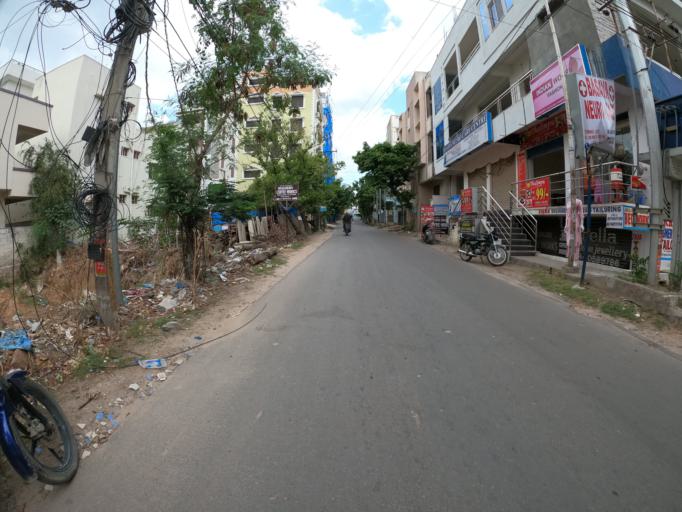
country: IN
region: Telangana
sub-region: Hyderabad
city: Hyderabad
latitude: 17.4070
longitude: 78.3909
